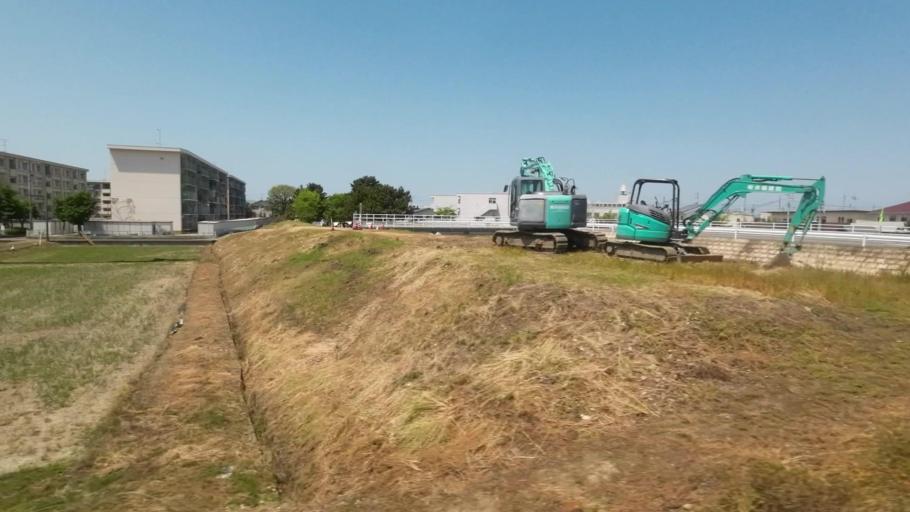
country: JP
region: Ehime
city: Hojo
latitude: 33.9464
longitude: 132.7717
